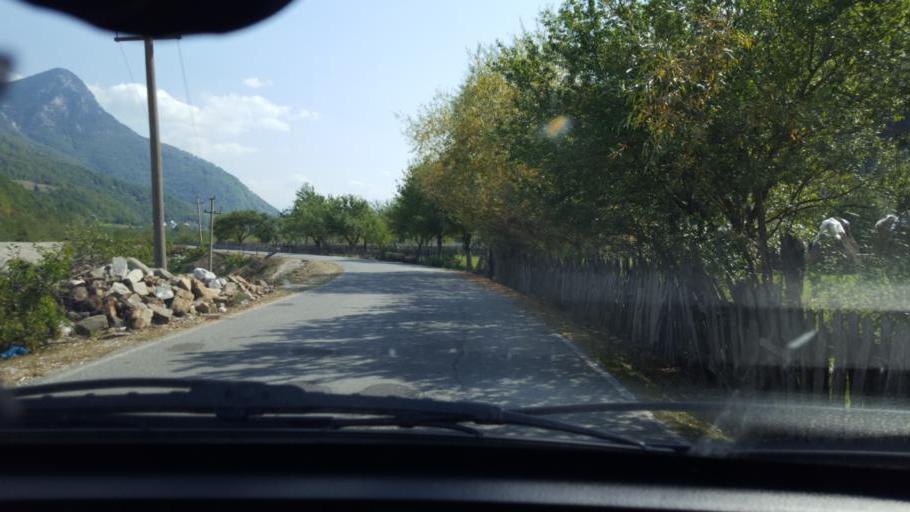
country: ME
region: Andrijevica
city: Andrijevica
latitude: 42.5893
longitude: 19.6968
